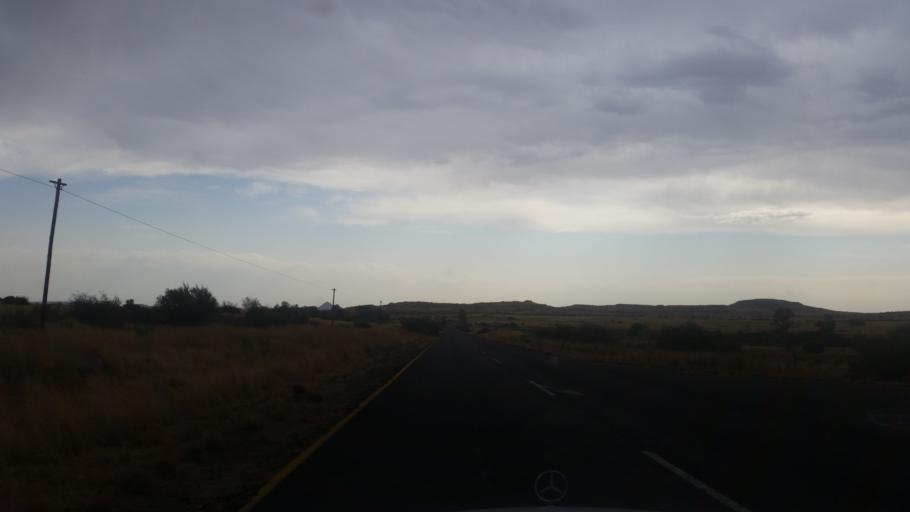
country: ZA
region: Eastern Cape
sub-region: Joe Gqabi District Municipality
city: Aliwal North
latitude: -30.4027
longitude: 26.2243
